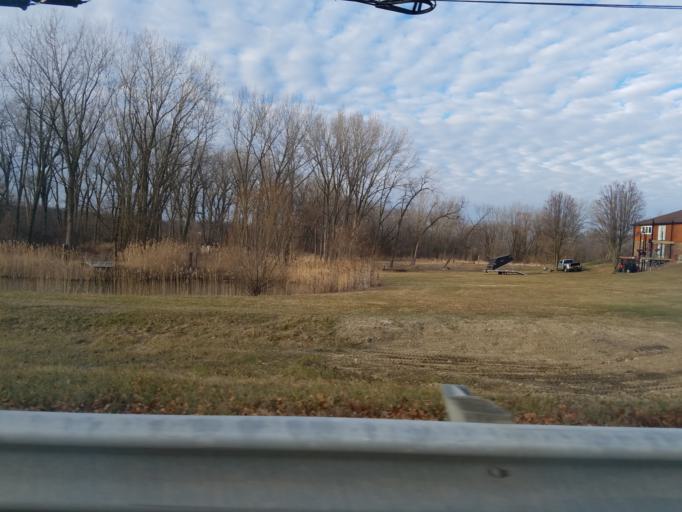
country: US
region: Illinois
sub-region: Will County
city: New Lenox
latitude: 41.5320
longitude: -87.9359
